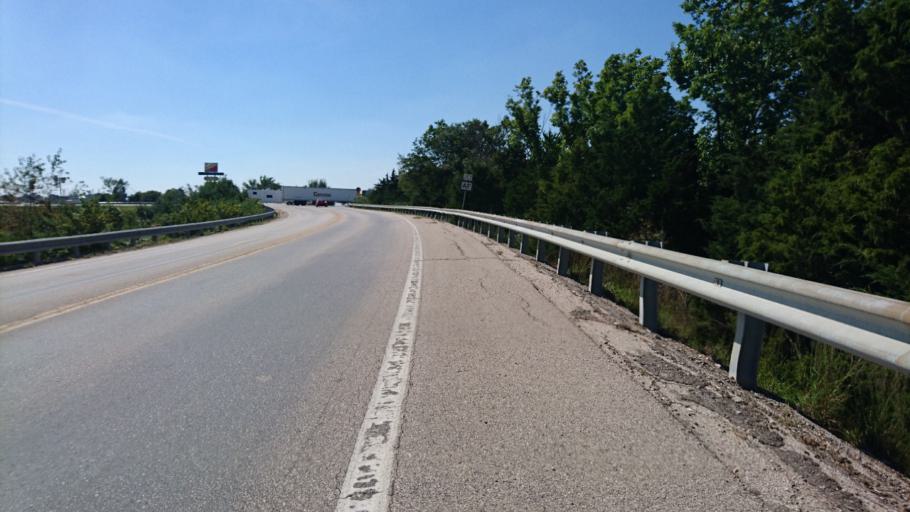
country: US
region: Missouri
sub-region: Franklin County
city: Sullivan
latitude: 38.2263
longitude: -91.1553
